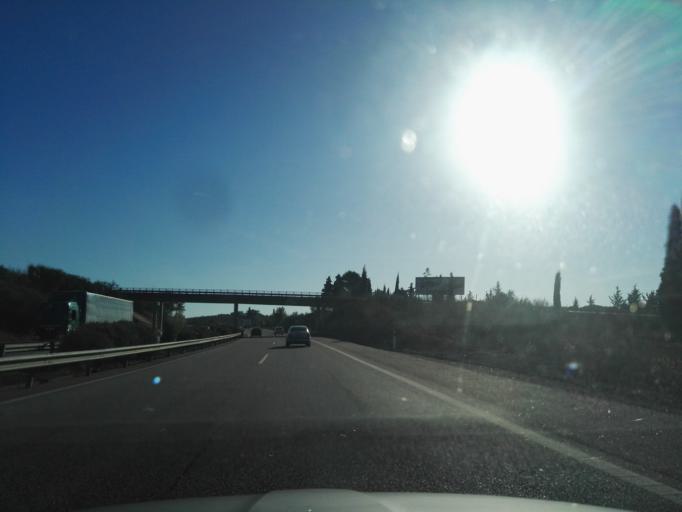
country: PT
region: Santarem
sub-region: Torres Novas
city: Torres Novas
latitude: 39.4715
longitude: -8.5930
